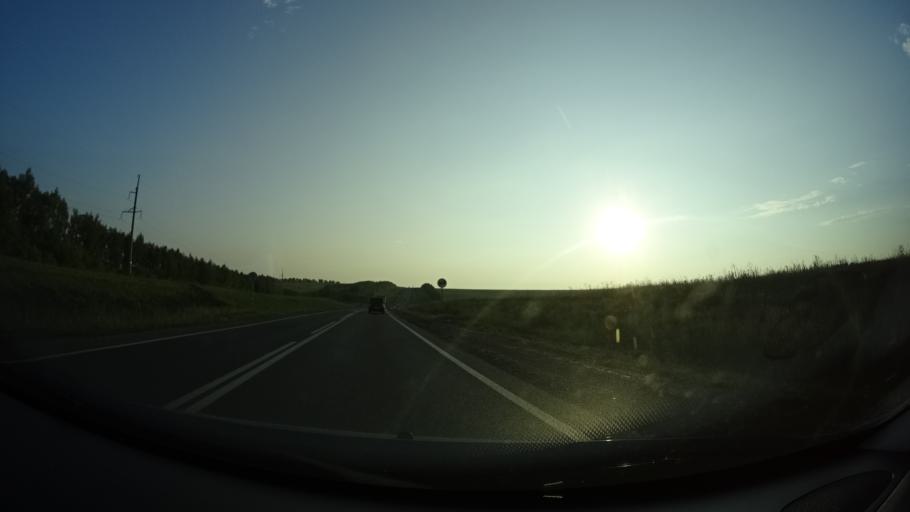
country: RU
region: Samara
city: Kamyshla
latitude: 54.0263
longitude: 51.8855
